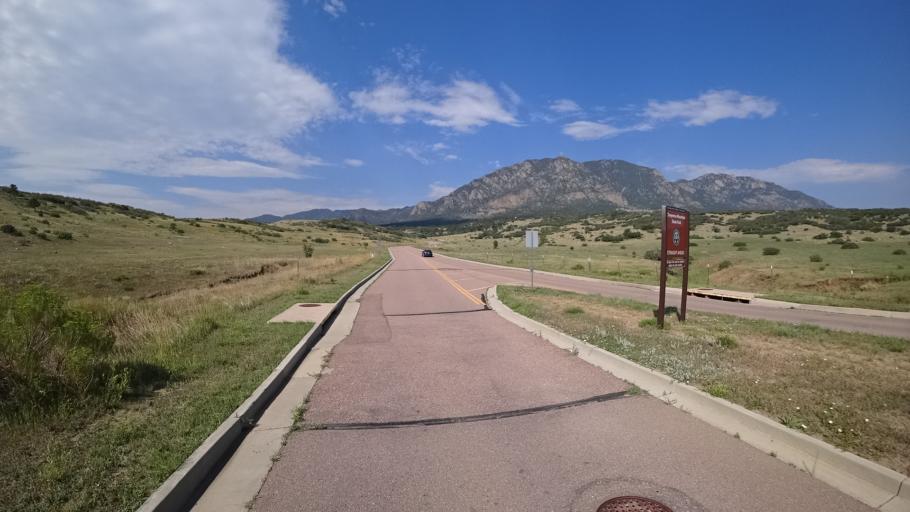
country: US
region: Colorado
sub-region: El Paso County
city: Fort Carson
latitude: 38.7376
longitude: -104.8118
